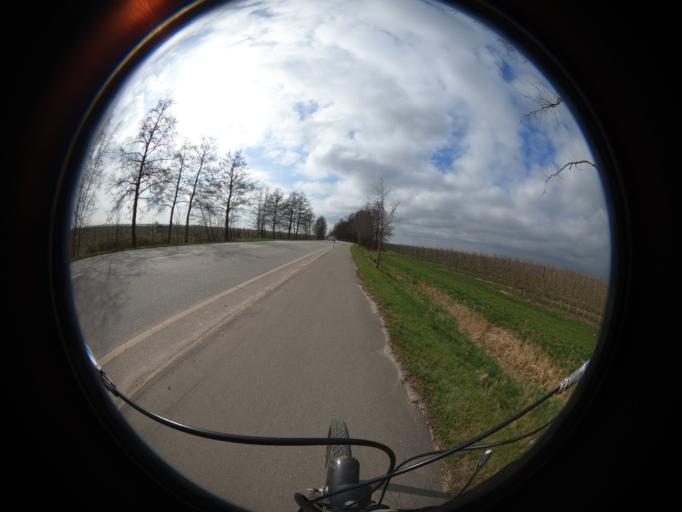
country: DE
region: Lower Saxony
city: Neu Wulmstorf
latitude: 53.5032
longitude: 9.7850
